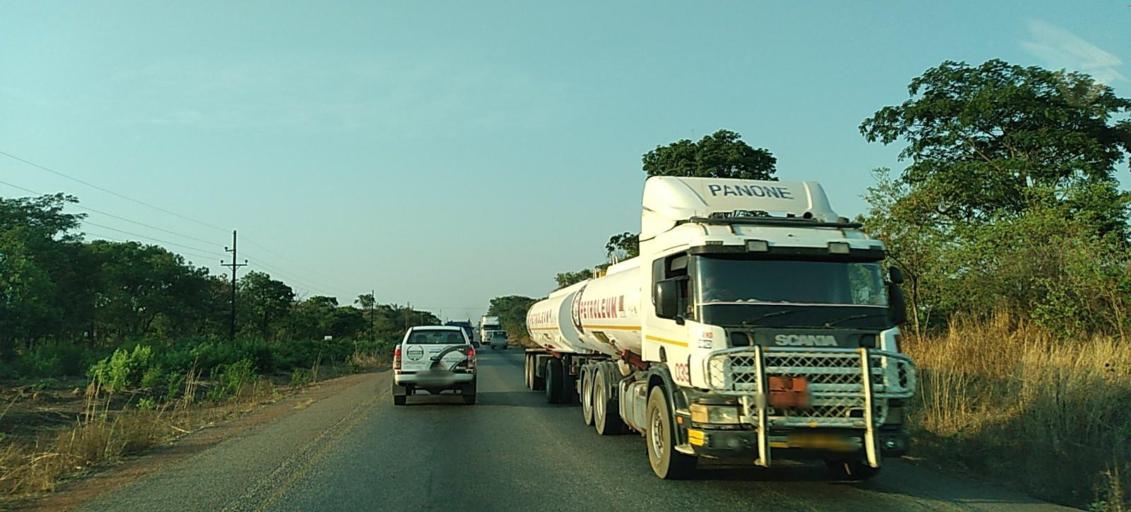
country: ZM
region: Copperbelt
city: Ndola
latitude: -13.1621
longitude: 28.6985
